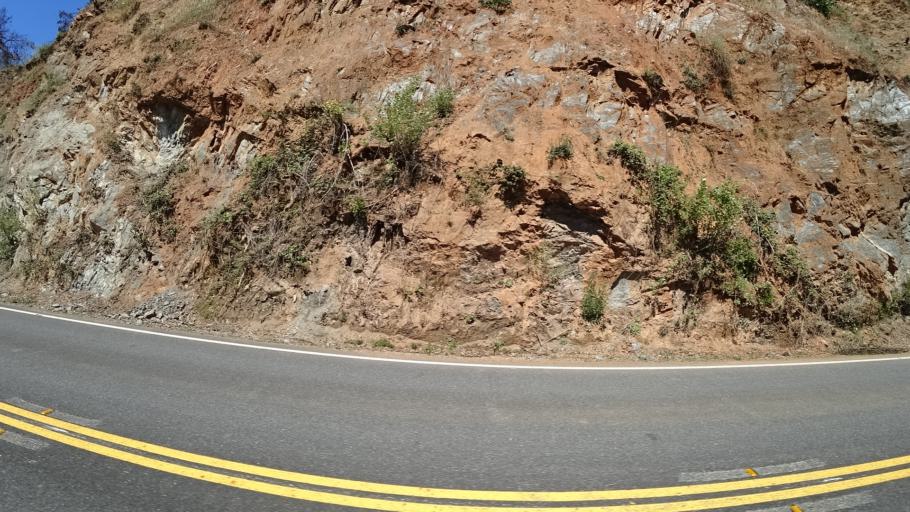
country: US
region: California
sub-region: Trinity County
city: Weaverville
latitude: 40.7648
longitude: -123.0773
